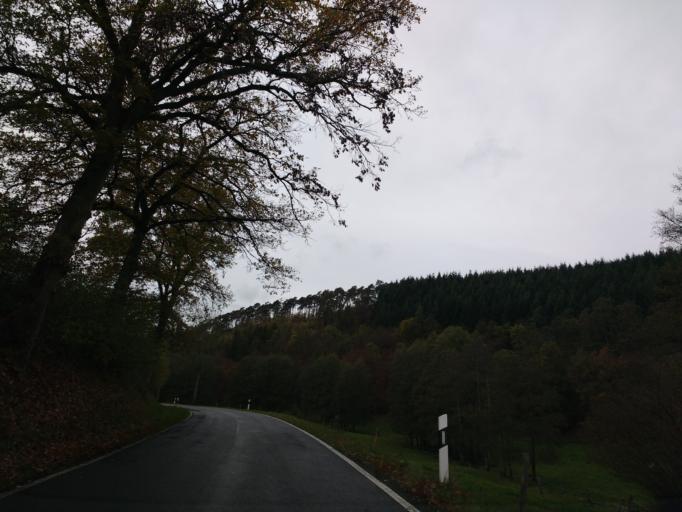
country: DE
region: Hesse
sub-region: Regierungsbezirk Kassel
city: Vohl
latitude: 51.1974
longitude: 8.9460
